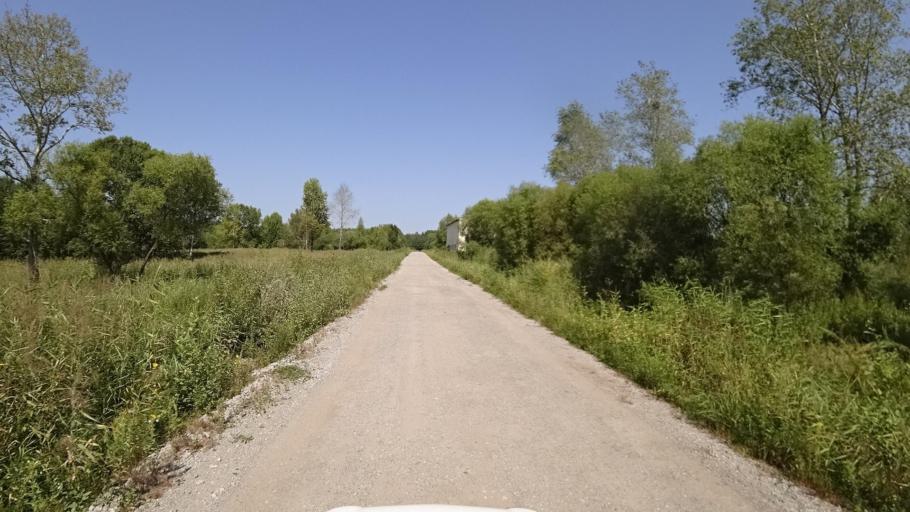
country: RU
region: Khabarovsk Krai
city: Khor
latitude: 47.9699
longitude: 135.1139
